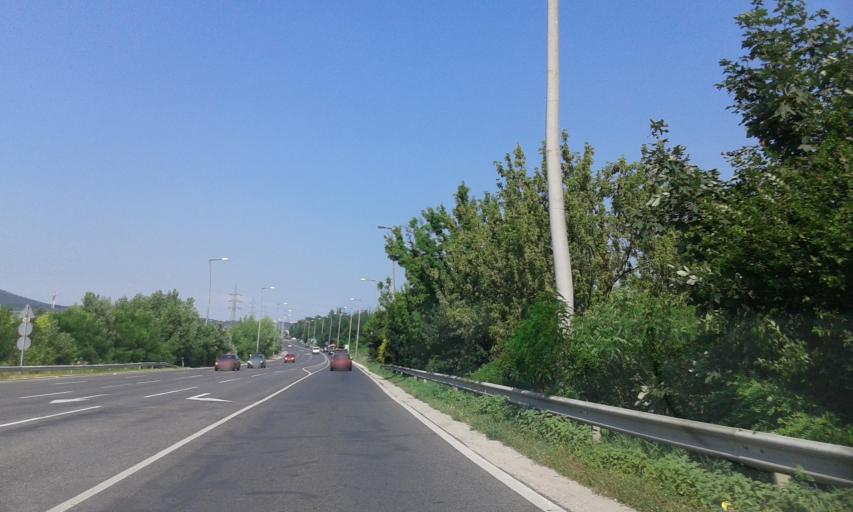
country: HU
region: Pest
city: Toeroekbalint
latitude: 47.4597
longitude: 18.9017
